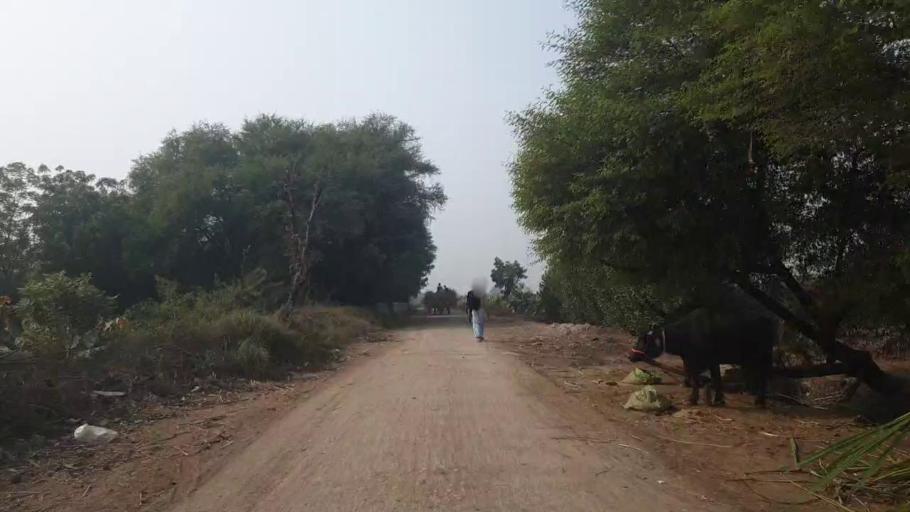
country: PK
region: Sindh
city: Bhit Shah
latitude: 25.7739
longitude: 68.5636
